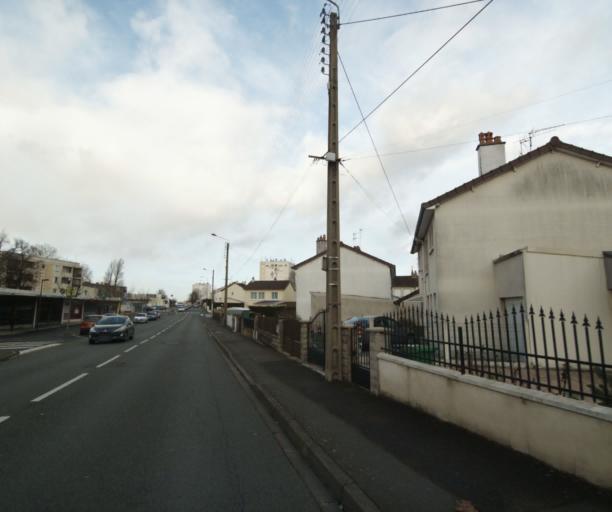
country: FR
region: Pays de la Loire
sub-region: Departement de la Sarthe
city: Le Mans
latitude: 47.9700
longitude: 0.2105
